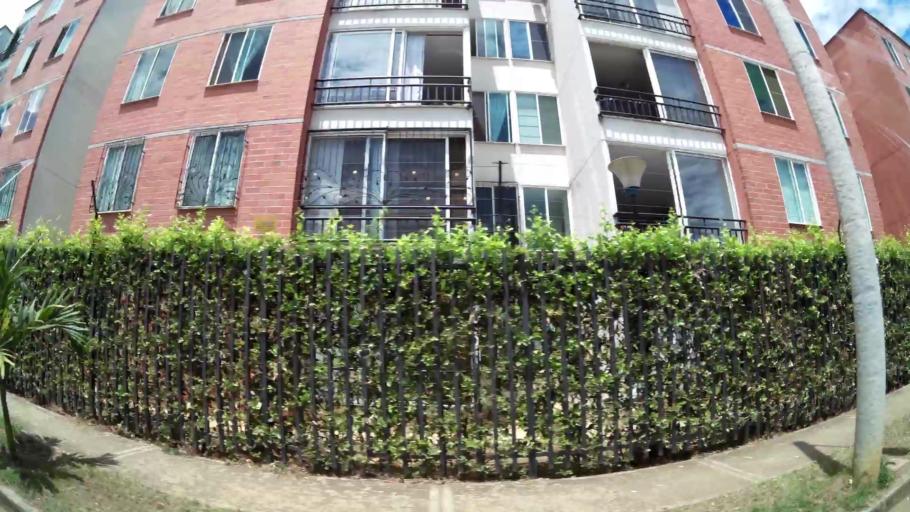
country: CO
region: Valle del Cauca
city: Cali
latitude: 3.3807
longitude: -76.5114
